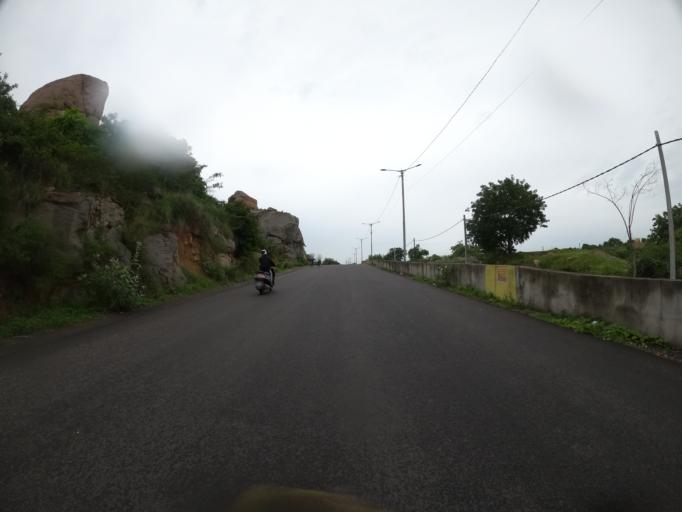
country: IN
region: Telangana
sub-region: Rangareddi
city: Kukatpalli
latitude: 17.4608
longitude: 78.3929
